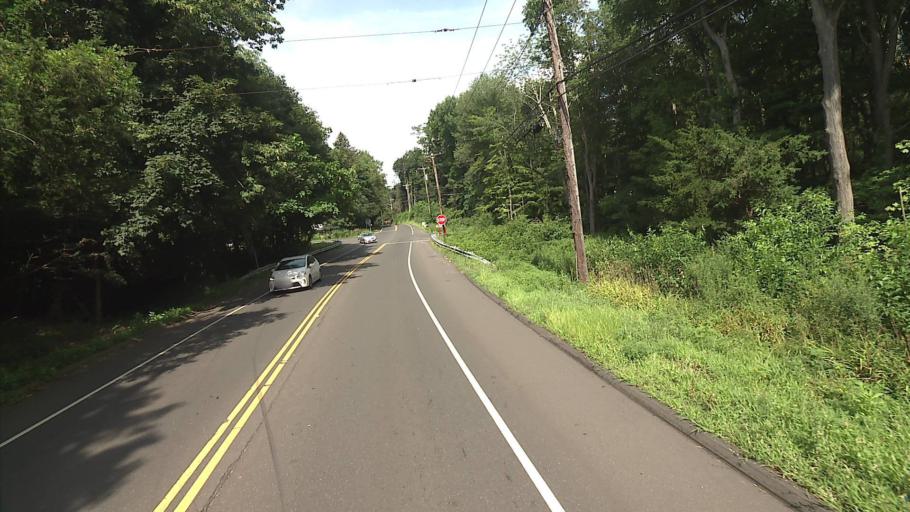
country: US
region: Connecticut
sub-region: New Haven County
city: Woodbridge
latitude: 41.3311
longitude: -73.0009
